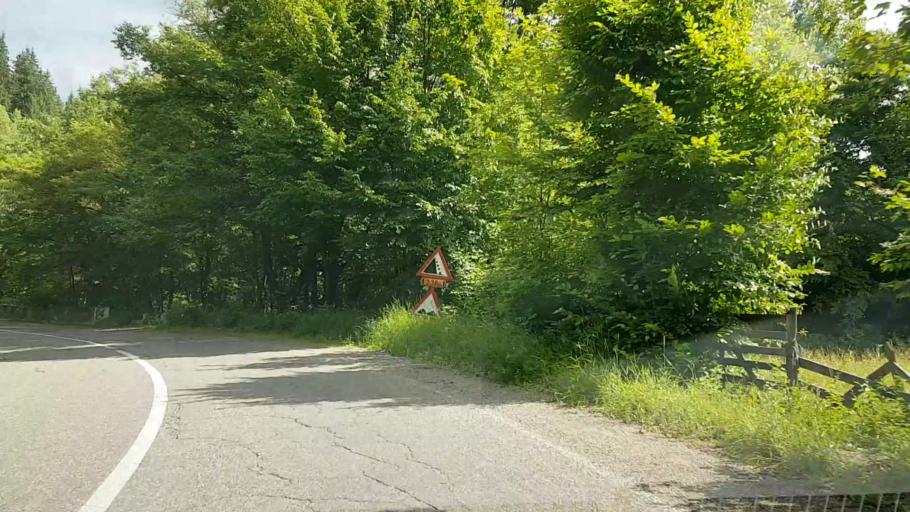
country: RO
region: Neamt
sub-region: Comuna Ceahlau
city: Ceahlau
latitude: 47.0581
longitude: 25.9696
